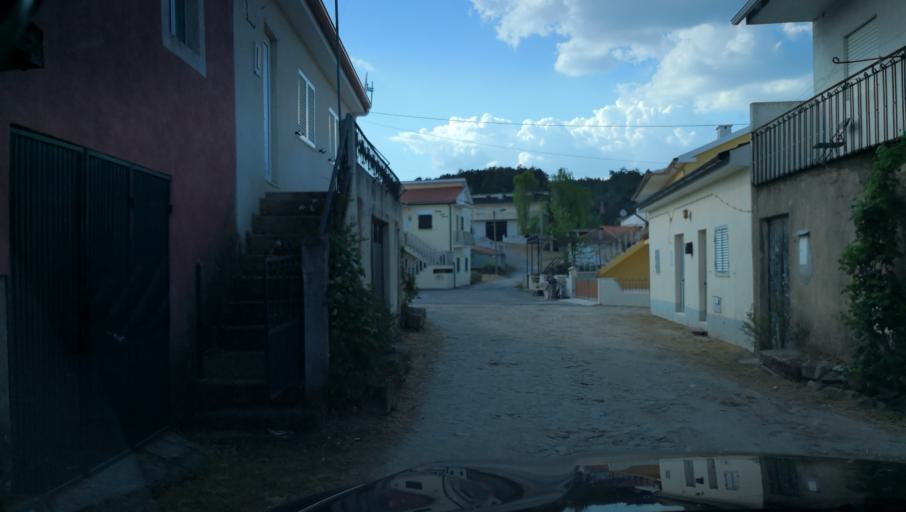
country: PT
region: Vila Real
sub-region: Sabrosa
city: Vilela
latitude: 41.2406
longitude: -7.6515
